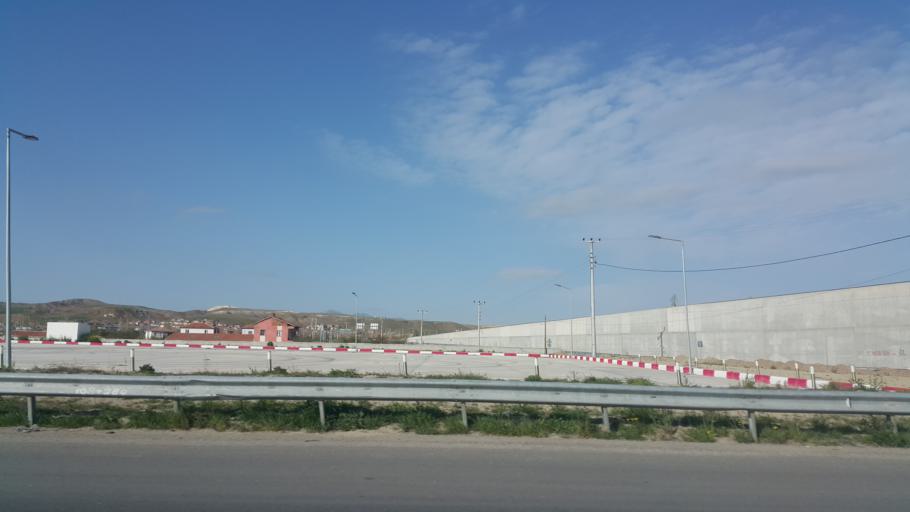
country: TR
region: Aksaray
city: Acipinar
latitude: 38.4758
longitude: 33.8979
